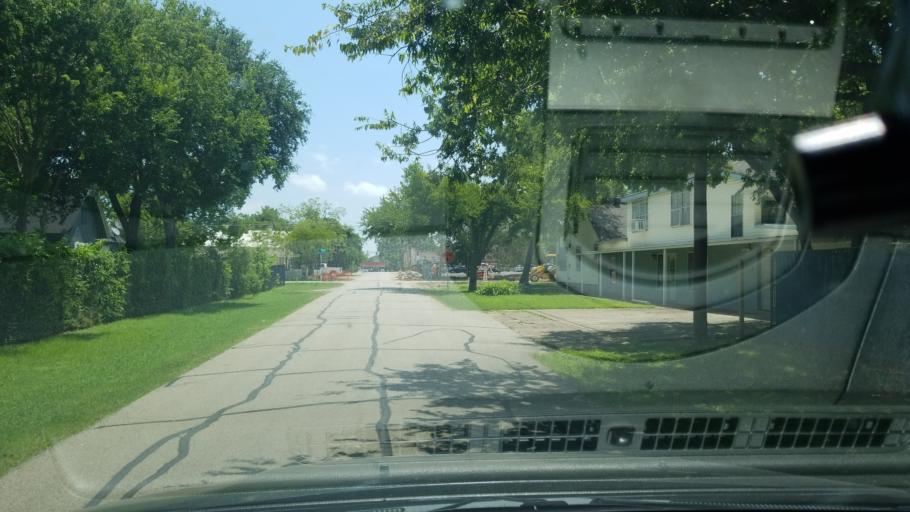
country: US
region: Texas
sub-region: Dallas County
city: Balch Springs
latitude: 32.7325
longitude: -96.6855
